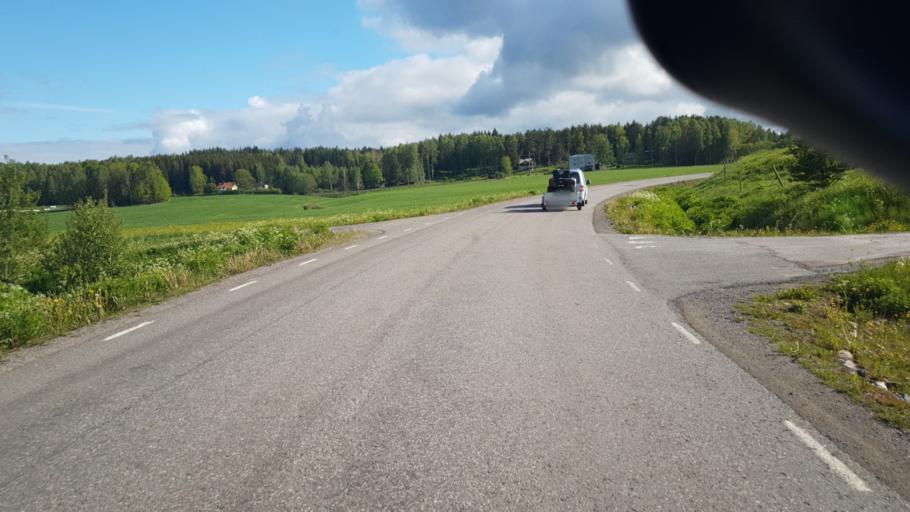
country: SE
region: Vaermland
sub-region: Eda Kommun
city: Charlottenberg
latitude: 59.7986
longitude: 12.2190
